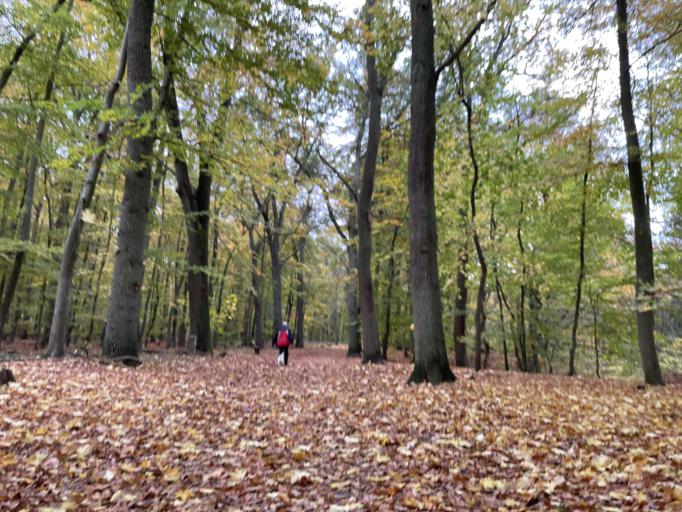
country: DE
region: Lower Saxony
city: Lueneburg
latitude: 53.2234
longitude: 10.3965
